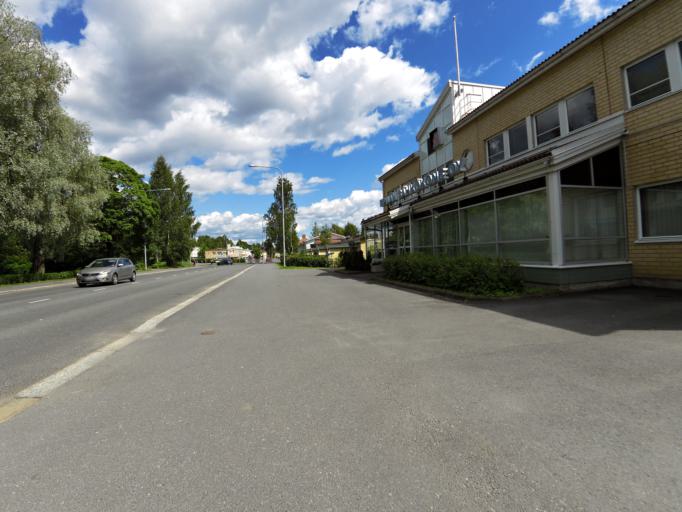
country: FI
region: Pirkanmaa
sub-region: Tampere
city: Pirkkala
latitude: 61.5076
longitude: 23.6662
